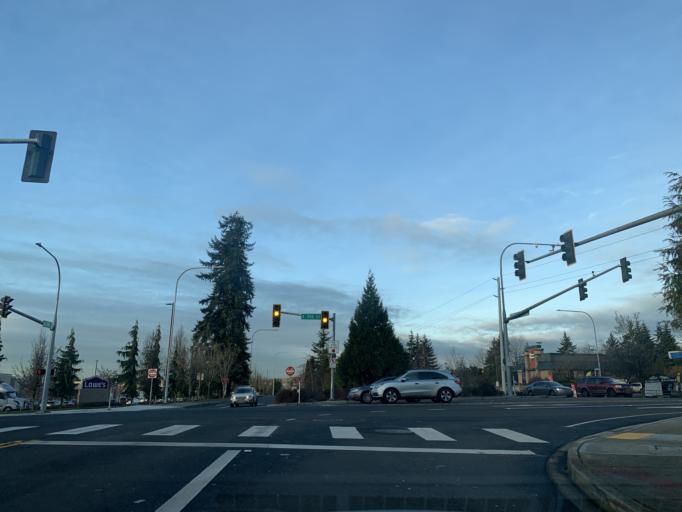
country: US
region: Washington
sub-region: King County
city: Lakeland South
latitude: 47.2824
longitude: -122.3136
